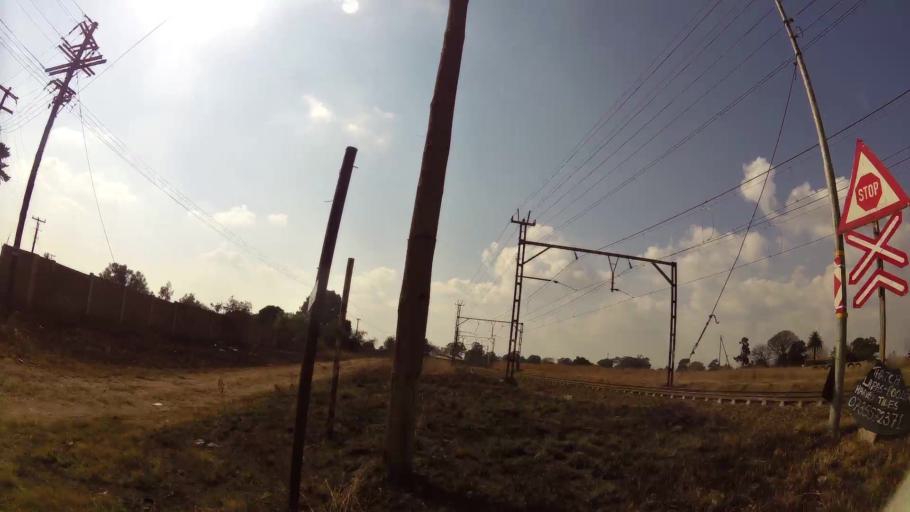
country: ZA
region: Mpumalanga
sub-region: Nkangala District Municipality
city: Delmas
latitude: -26.1896
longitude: 28.5401
